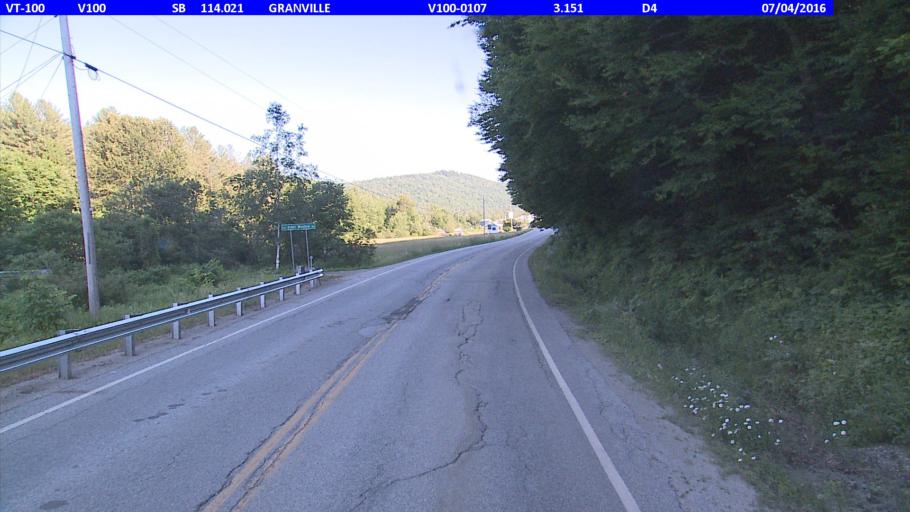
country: US
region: Vermont
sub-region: Orange County
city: Randolph
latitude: 43.9874
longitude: -72.8496
